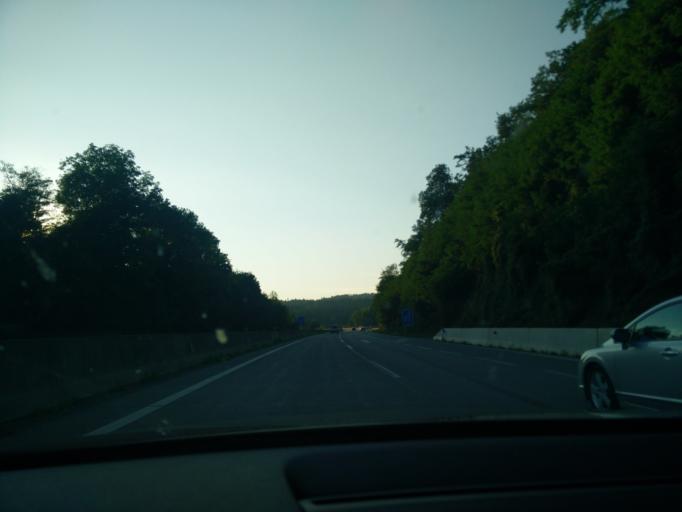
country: AT
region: Carinthia
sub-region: Klagenfurt am Woerthersee
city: Klagenfurt am Woerthersee
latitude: 46.6263
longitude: 14.2462
